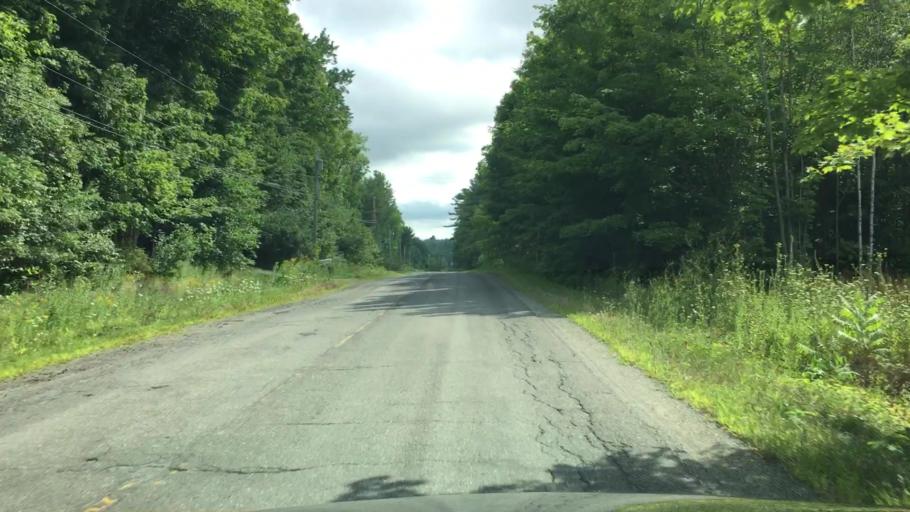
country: US
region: Maine
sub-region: Penobscot County
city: Hampden
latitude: 44.7235
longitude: -68.8655
